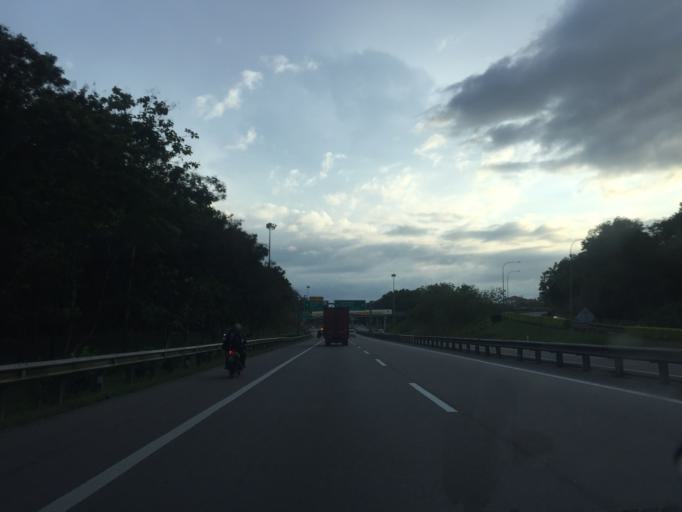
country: MY
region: Kedah
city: Sungai Petani
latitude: 5.6770
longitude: 100.5164
